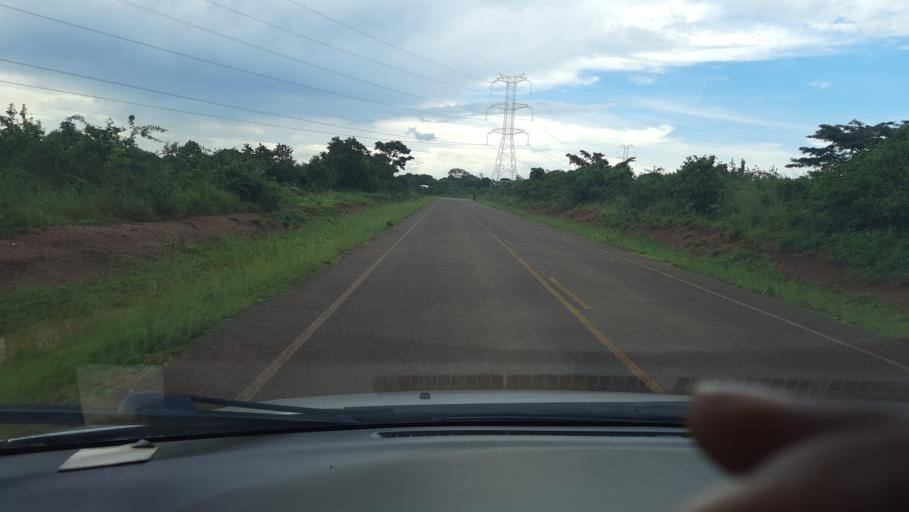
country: UG
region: Central Region
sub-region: Nakasongola District
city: Nakasongola
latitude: 1.3240
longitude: 32.4290
